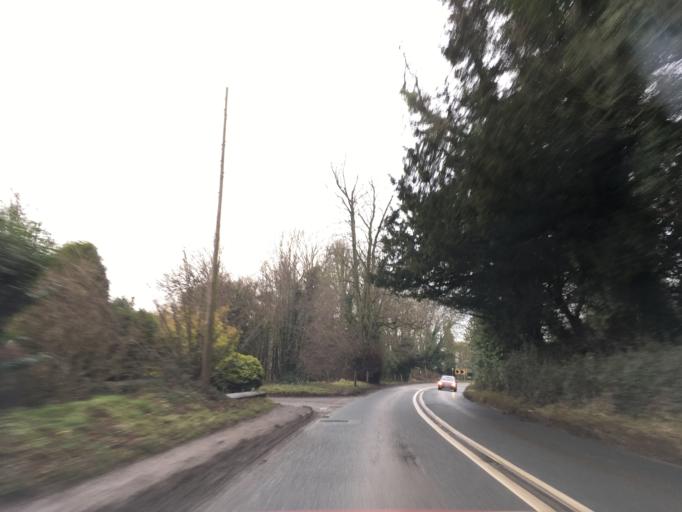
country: GB
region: England
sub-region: Gloucestershire
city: Tetbury
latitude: 51.6377
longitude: -2.1728
